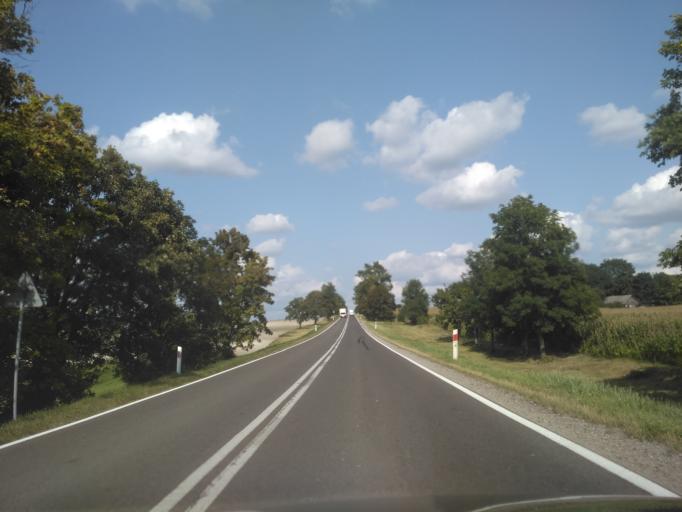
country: PL
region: Lublin Voivodeship
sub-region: Powiat chelmski
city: Rejowiec
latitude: 51.1012
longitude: 23.3034
